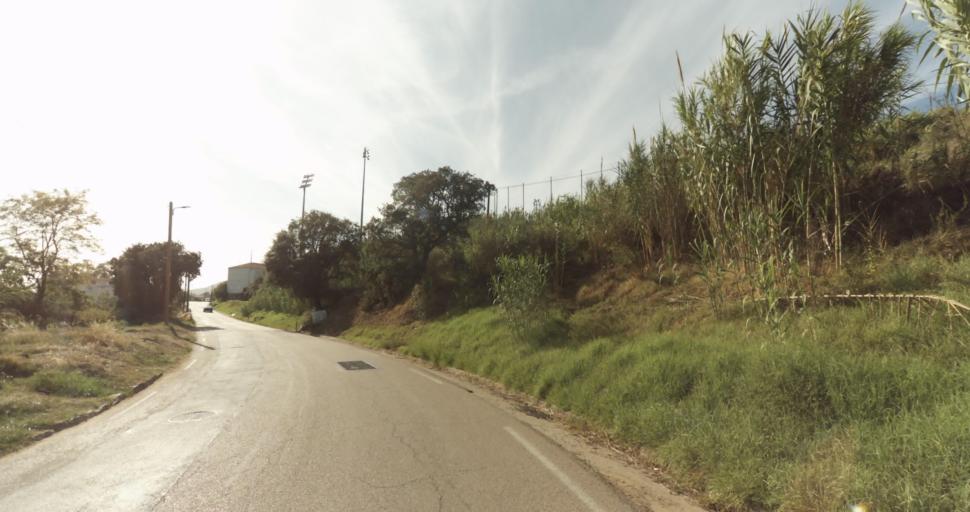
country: FR
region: Corsica
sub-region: Departement de la Corse-du-Sud
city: Ajaccio
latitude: 41.9306
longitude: 8.7795
